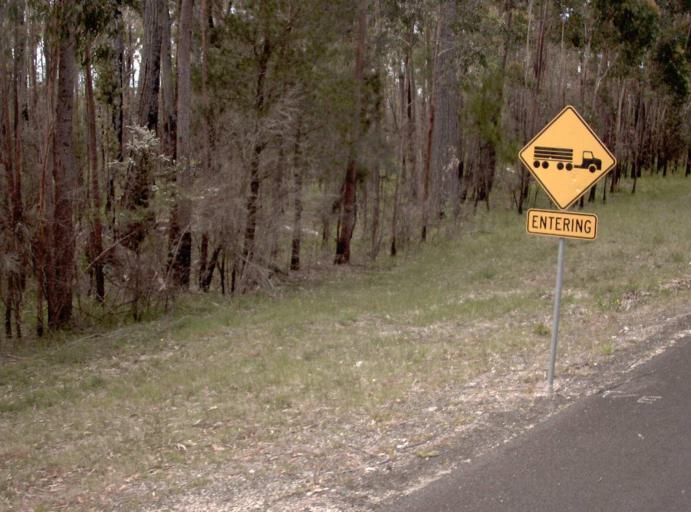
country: AU
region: New South Wales
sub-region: Bega Valley
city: Eden
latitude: -37.5122
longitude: 149.5123
